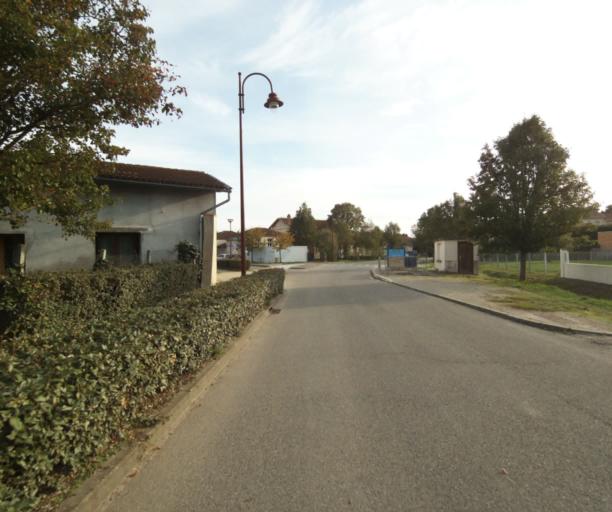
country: FR
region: Midi-Pyrenees
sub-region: Departement du Tarn-et-Garonne
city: Campsas
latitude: 43.8955
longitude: 1.3272
